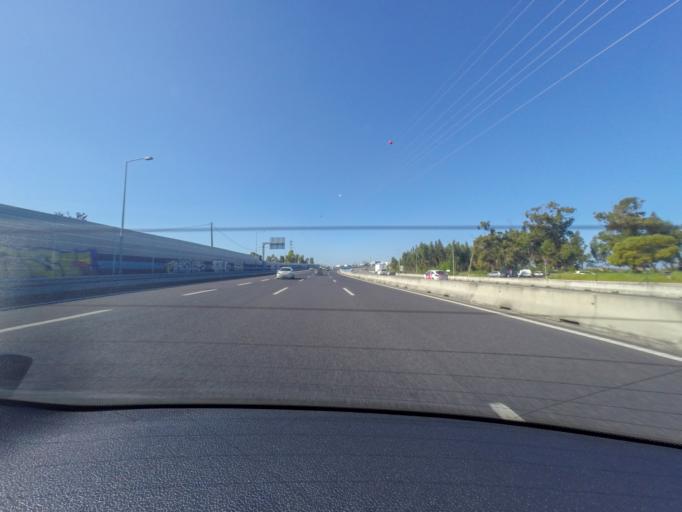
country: PT
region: Lisbon
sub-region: Cascais
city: Alcabideche
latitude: 38.7451
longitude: -9.3920
